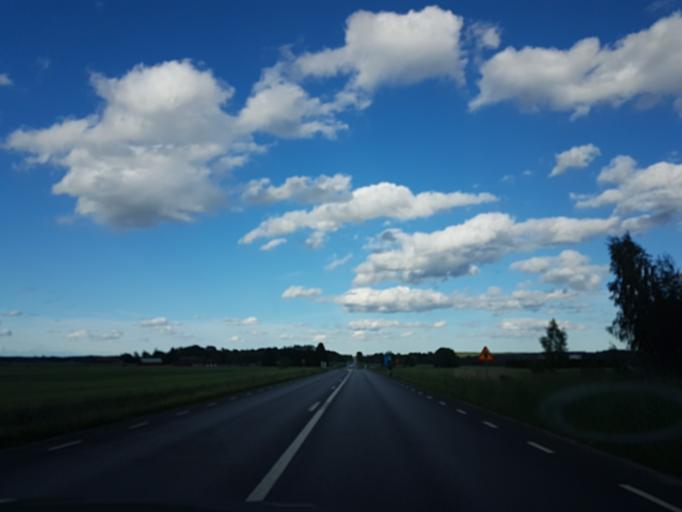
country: SE
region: Soedermanland
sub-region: Nykopings Kommun
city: Svalsta
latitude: 58.7410
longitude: 16.8373
